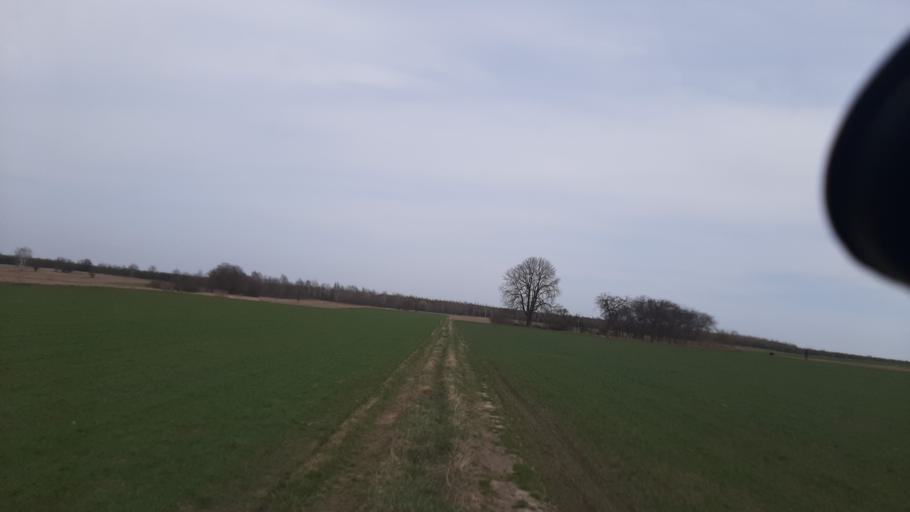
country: PL
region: Lublin Voivodeship
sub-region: Powiat lubelski
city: Jastkow
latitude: 51.3765
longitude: 22.4271
